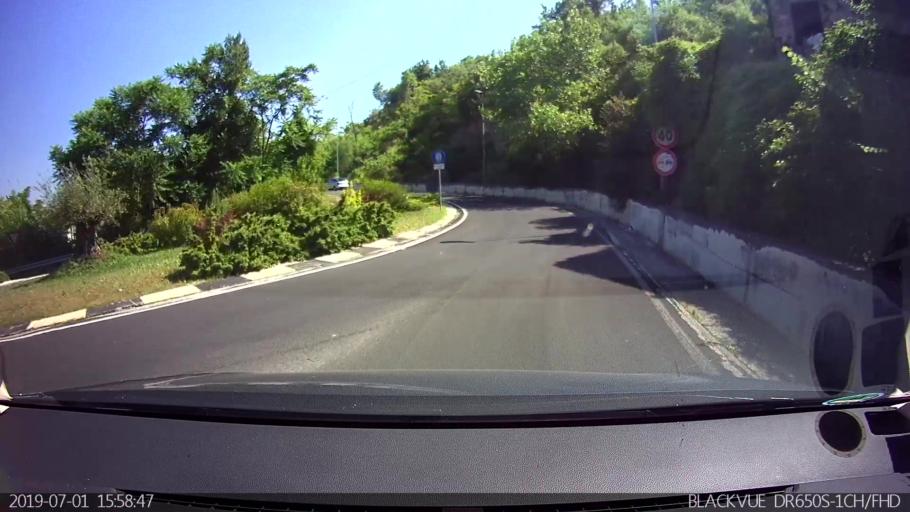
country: IT
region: Latium
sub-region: Provincia di Frosinone
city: Sant'Angelo in Villa-Giglio
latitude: 41.6653
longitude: 13.4243
